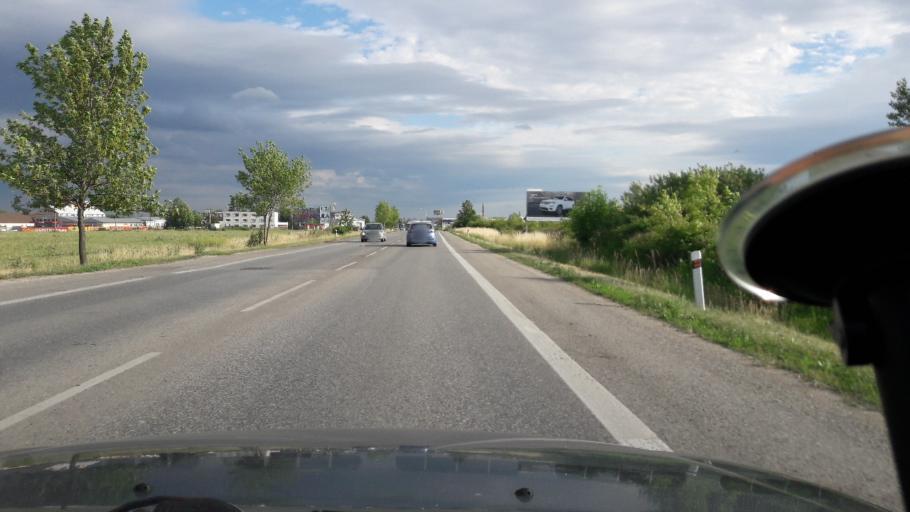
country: SK
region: Bratislavsky
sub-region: Okres Pezinok
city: Pezinok
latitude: 48.2958
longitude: 17.2810
